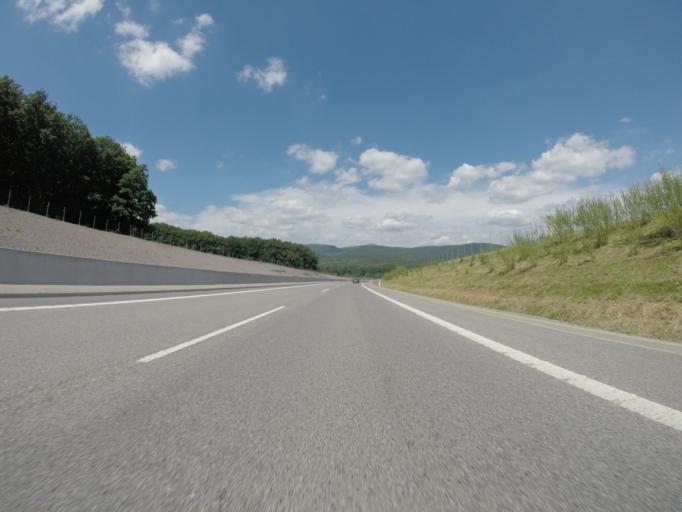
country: SK
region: Nitriansky
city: Tlmace
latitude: 48.3662
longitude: 18.5018
